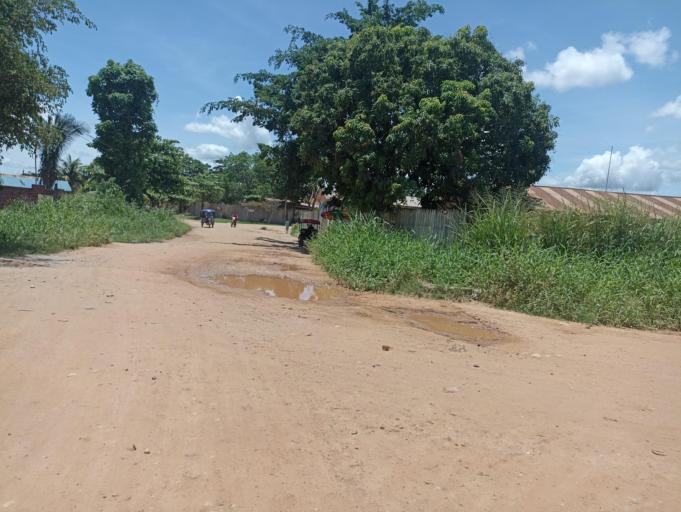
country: PE
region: Ucayali
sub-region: Provincia de Coronel Portillo
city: Puerto Callao
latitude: -8.3630
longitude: -74.5906
